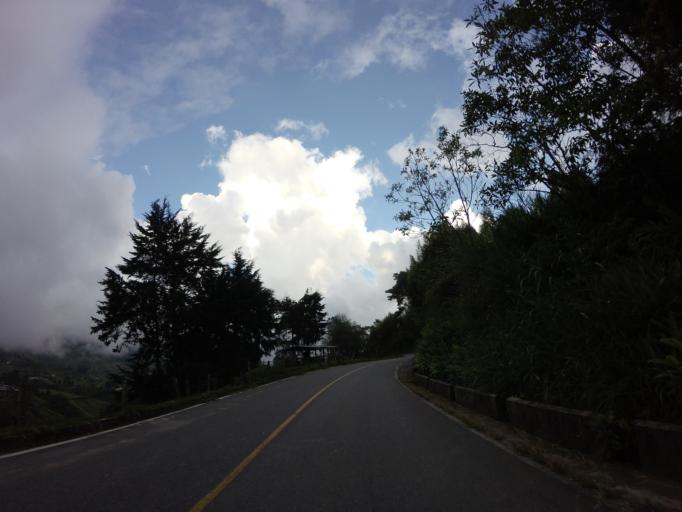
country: CO
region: Caldas
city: Pensilvania
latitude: 5.3785
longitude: -75.1570
